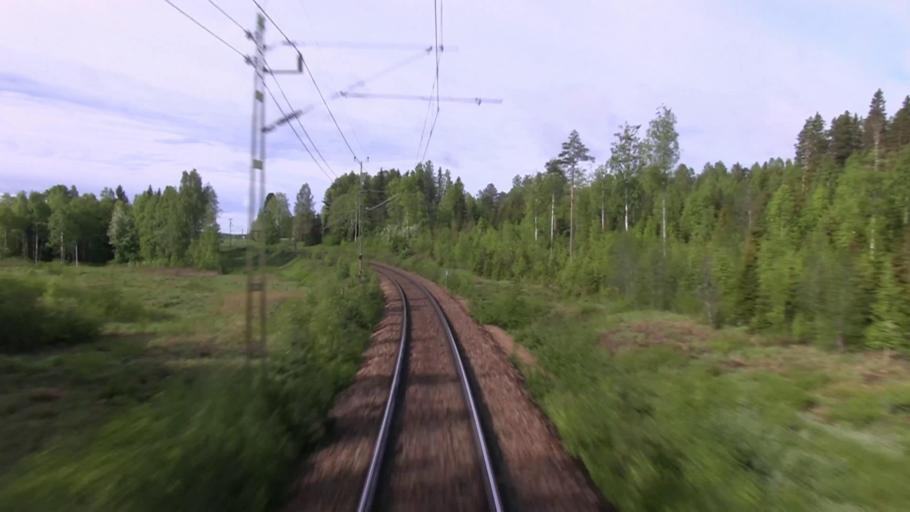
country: SE
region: Vaesterbotten
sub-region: Vindelns Kommun
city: Vindeln
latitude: 64.1090
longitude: 19.6867
